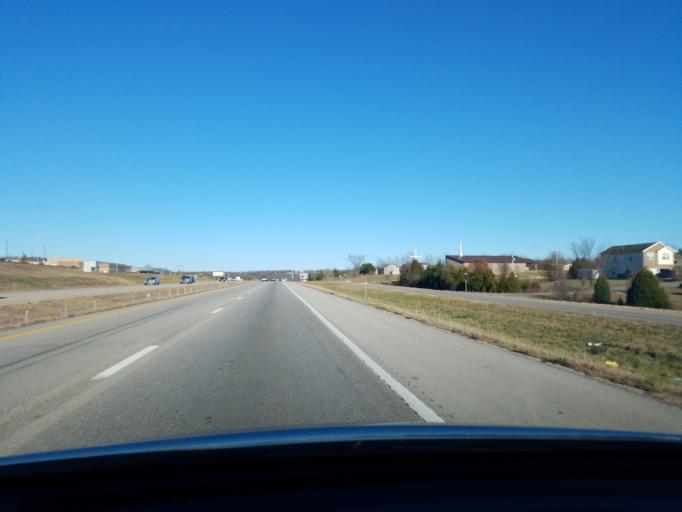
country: US
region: Missouri
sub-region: Pulaski County
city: Waynesville
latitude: 37.8079
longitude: -92.2163
